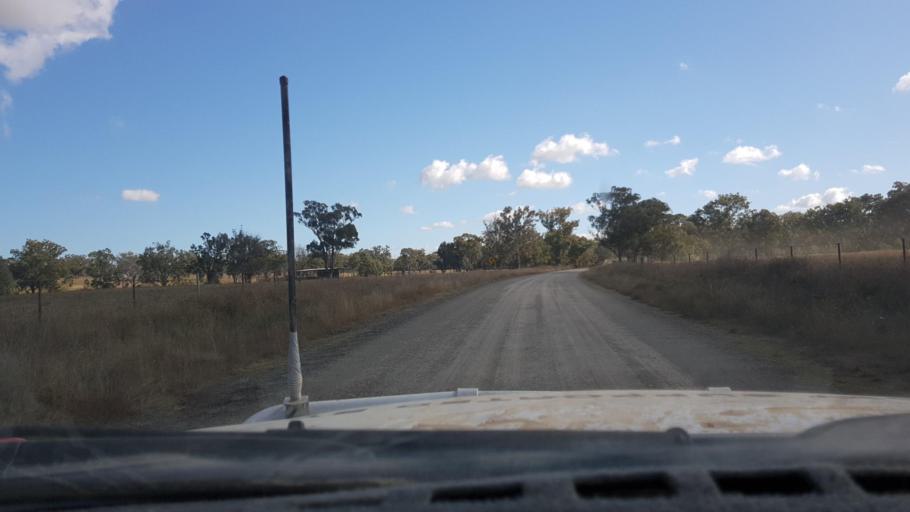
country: AU
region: New South Wales
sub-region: Tamworth Municipality
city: Manilla
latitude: -30.6023
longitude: 150.4993
